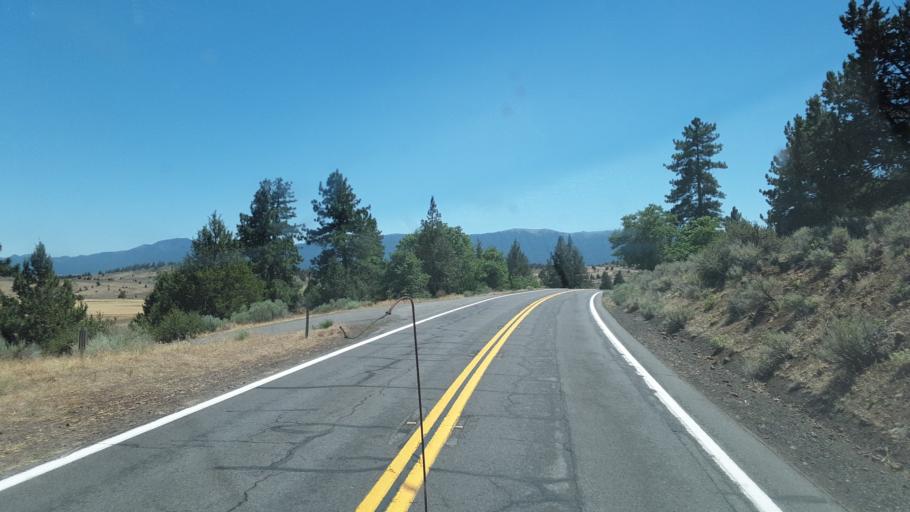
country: US
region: California
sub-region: Lassen County
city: Susanville
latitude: 40.4611
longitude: -120.6177
